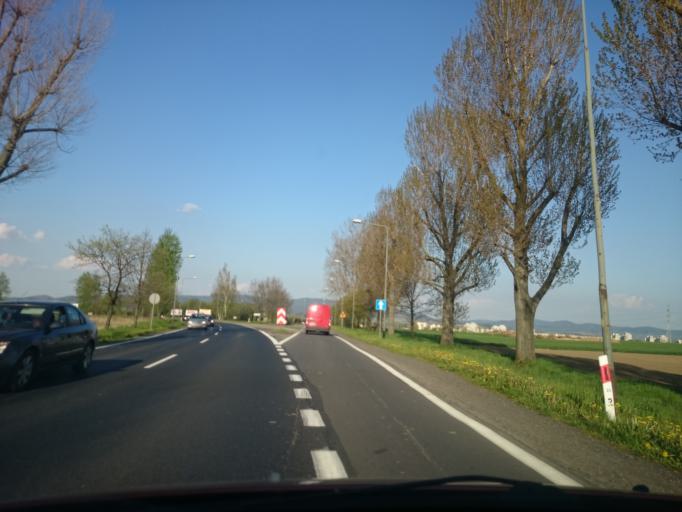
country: PL
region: Lower Silesian Voivodeship
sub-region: Powiat klodzki
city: Klodzko
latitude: 50.4382
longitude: 16.6222
